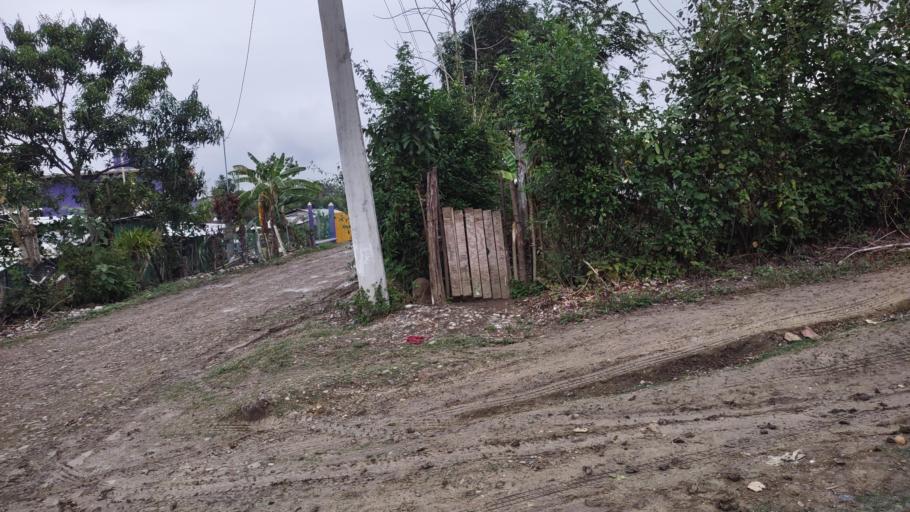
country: MX
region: Veracruz
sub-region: Papantla
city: El Chote
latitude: 20.3944
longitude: -97.3972
